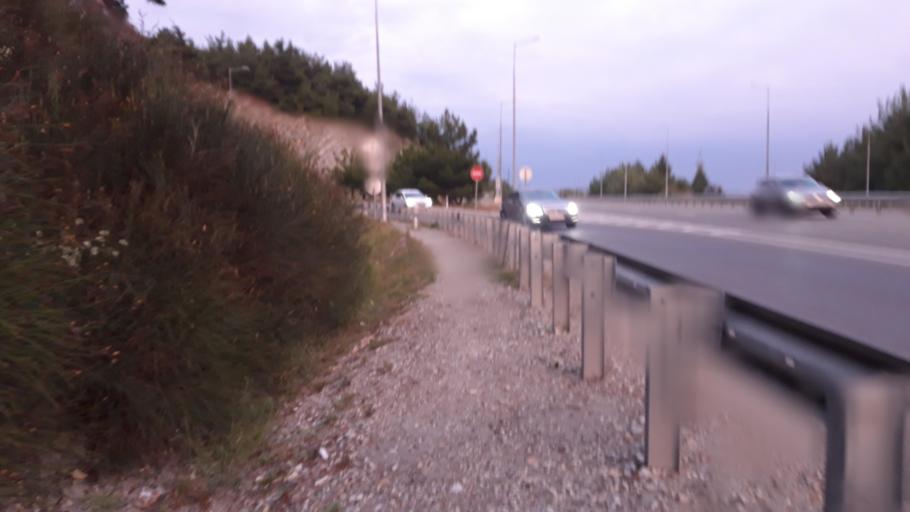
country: RU
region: Krasnodarskiy
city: Gelendzhik
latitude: 44.5776
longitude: 38.0895
